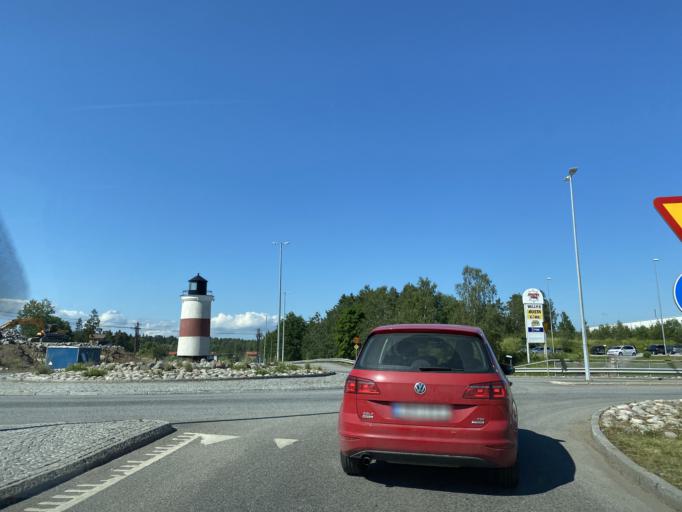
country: SE
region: Stockholm
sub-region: Norrtalje Kommun
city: Norrtalje
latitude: 59.7659
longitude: 18.6916
